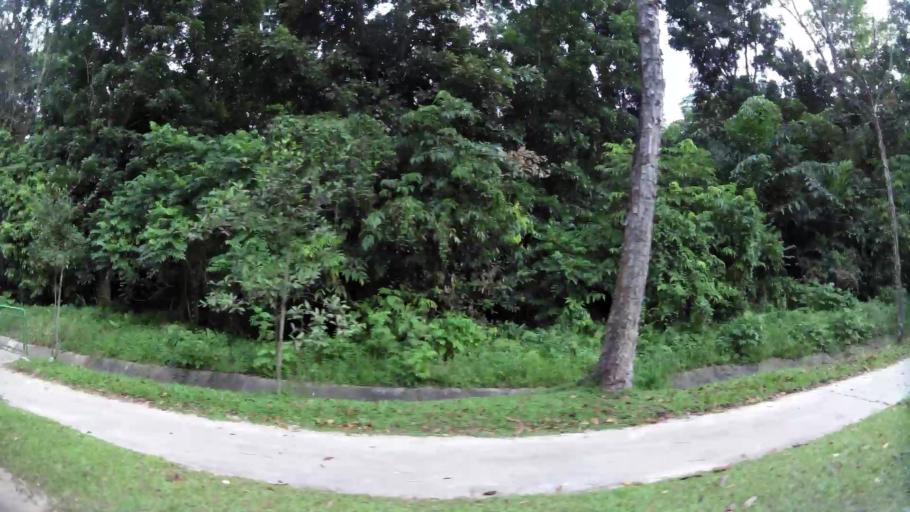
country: MY
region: Johor
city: Johor Bahru
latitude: 1.4176
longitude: 103.7013
